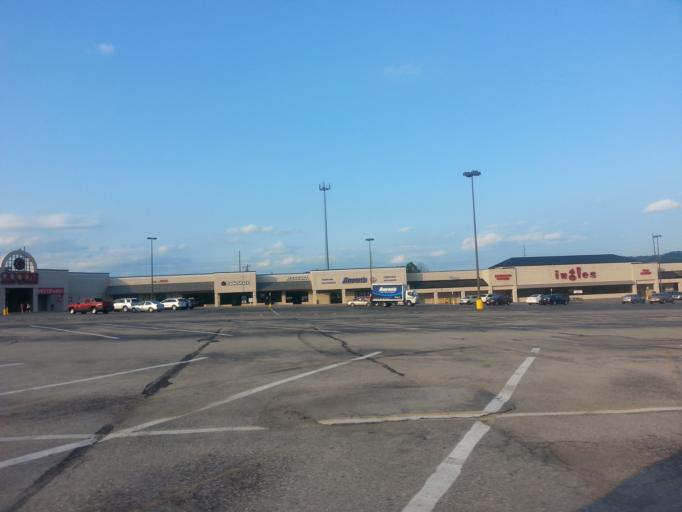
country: US
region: Tennessee
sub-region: Knox County
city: Knoxville
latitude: 36.0836
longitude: -83.9307
